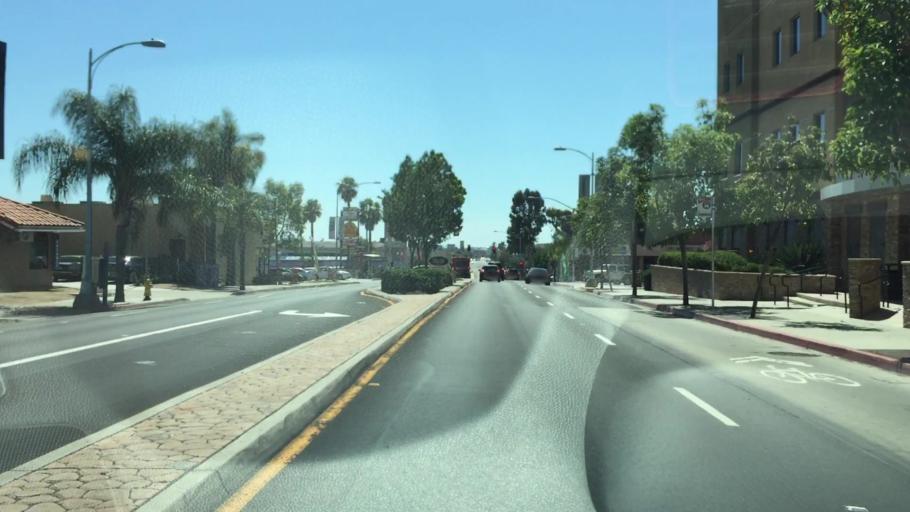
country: US
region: California
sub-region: San Diego County
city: Lemon Grove
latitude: 32.7581
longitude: -117.0776
